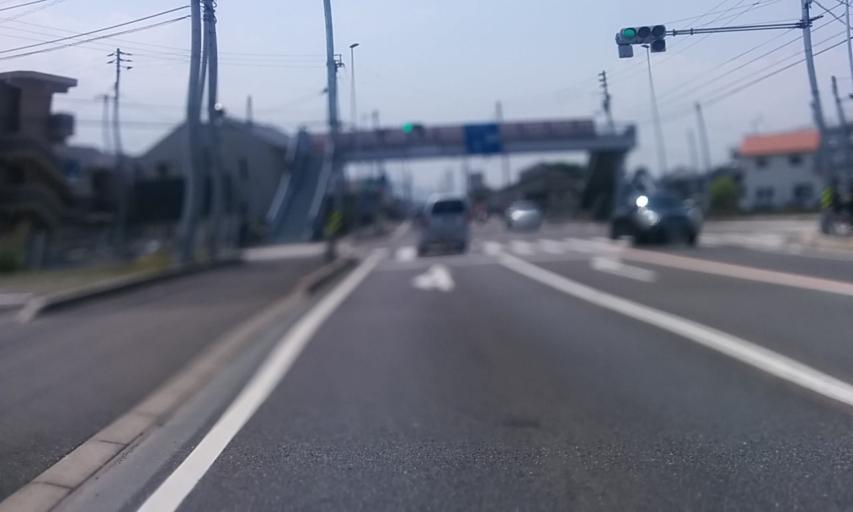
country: JP
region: Ehime
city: Saijo
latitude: 33.9078
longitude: 133.1905
